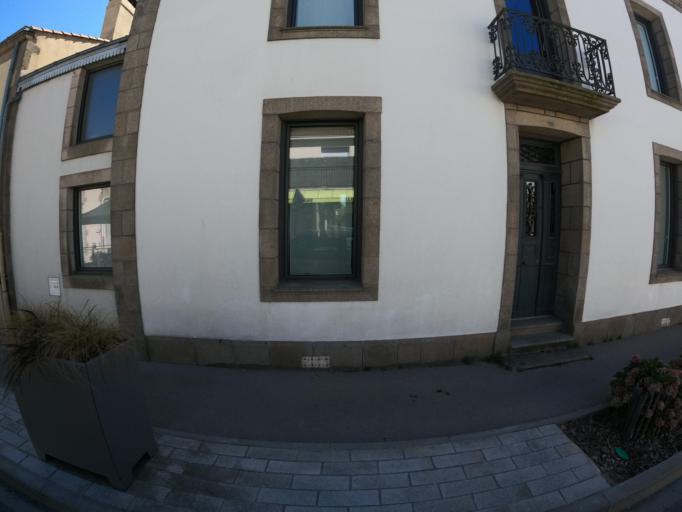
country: FR
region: Pays de la Loire
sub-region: Departement de la Vendee
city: Les Landes-Genusson
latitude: 46.9630
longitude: -1.1179
